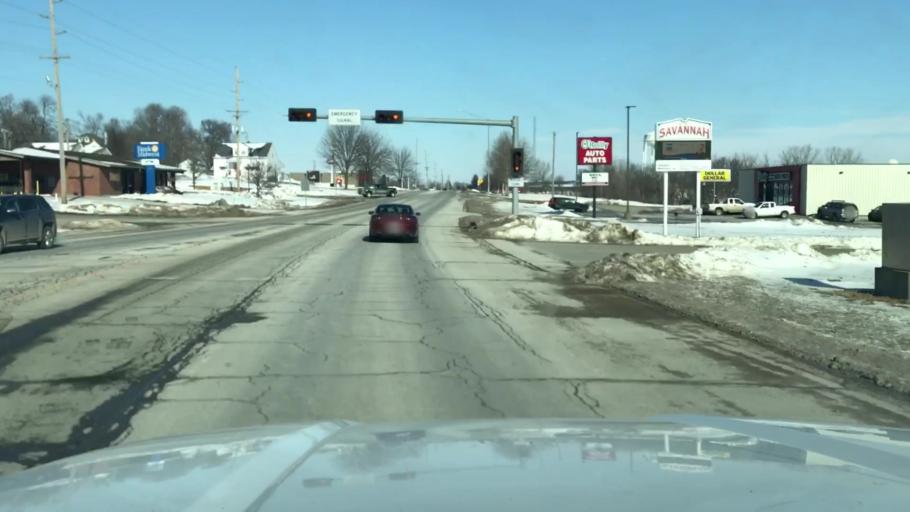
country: US
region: Missouri
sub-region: Andrew County
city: Savannah
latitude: 39.9404
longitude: -94.8218
